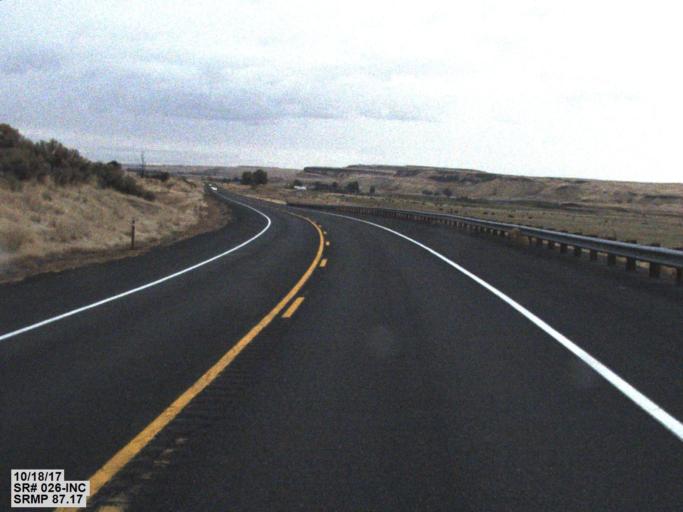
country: US
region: Washington
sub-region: Adams County
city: Ritzville
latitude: 46.7417
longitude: -118.2264
